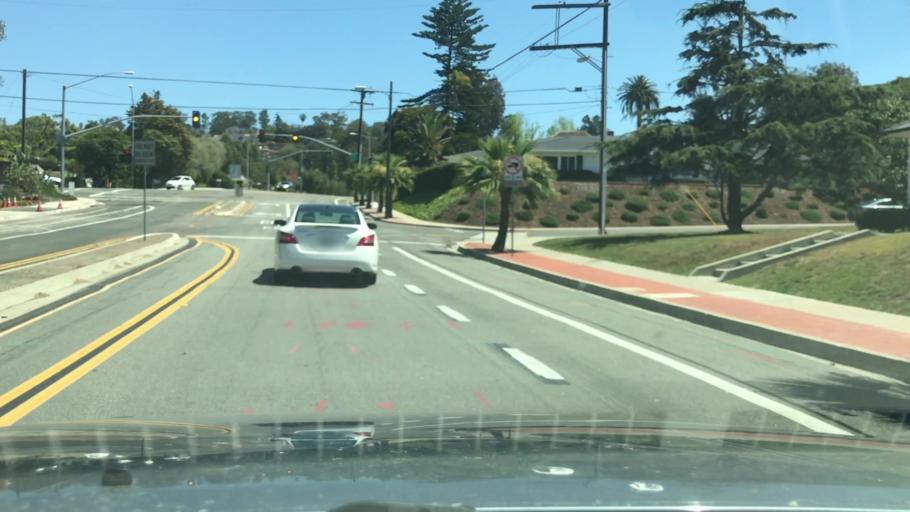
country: US
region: California
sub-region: San Diego County
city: La Jolla
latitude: 32.8323
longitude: -117.2649
